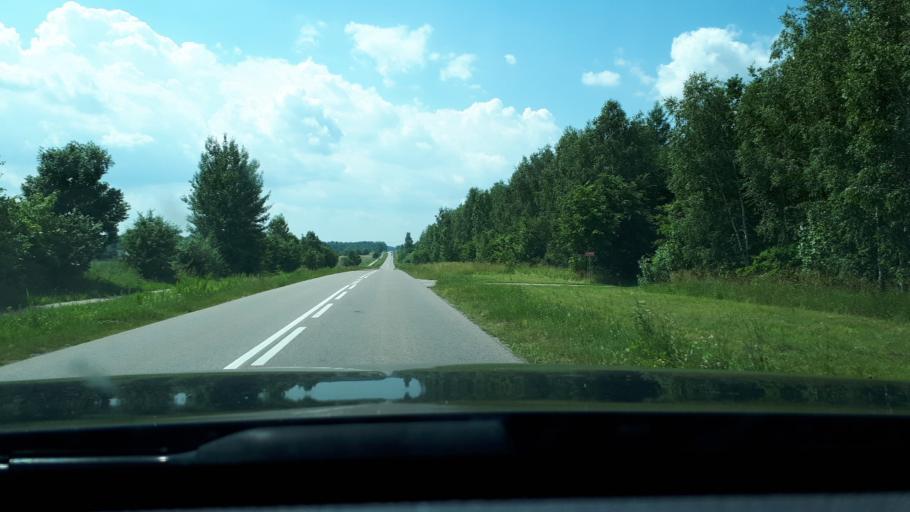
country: PL
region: Podlasie
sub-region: Powiat bialostocki
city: Choroszcz
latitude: 53.1287
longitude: 23.0083
